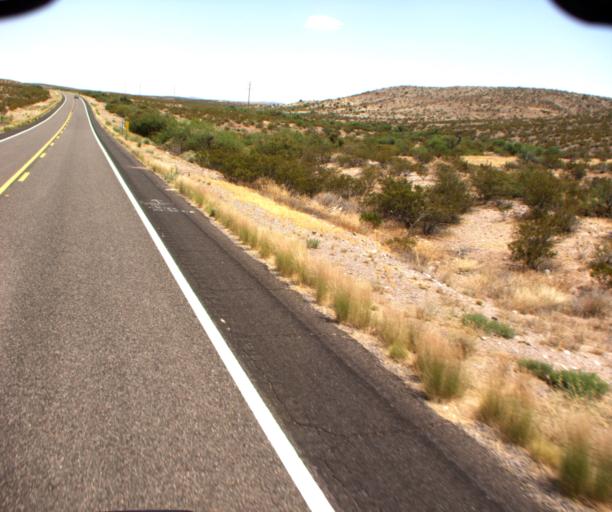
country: US
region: Arizona
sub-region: Graham County
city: Swift Trail Junction
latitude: 32.7510
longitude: -109.4032
